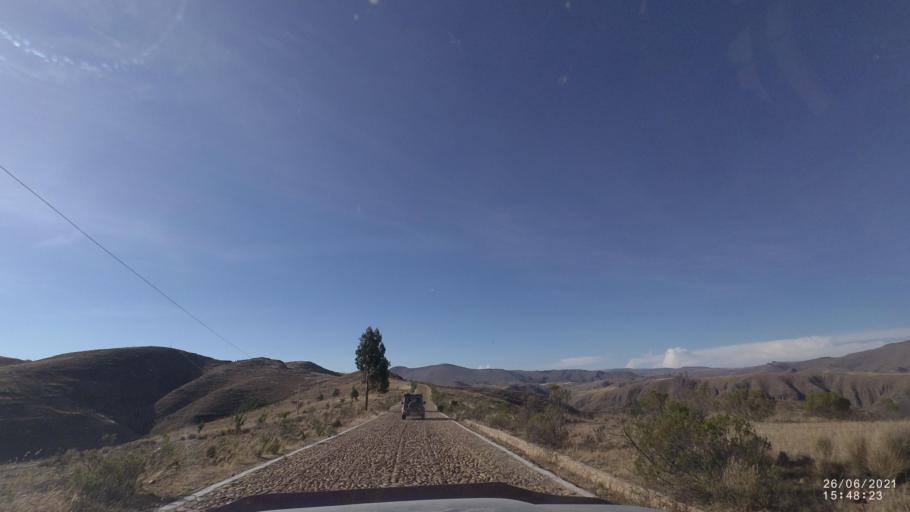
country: BO
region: Cochabamba
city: Arani
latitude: -17.8635
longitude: -65.6962
